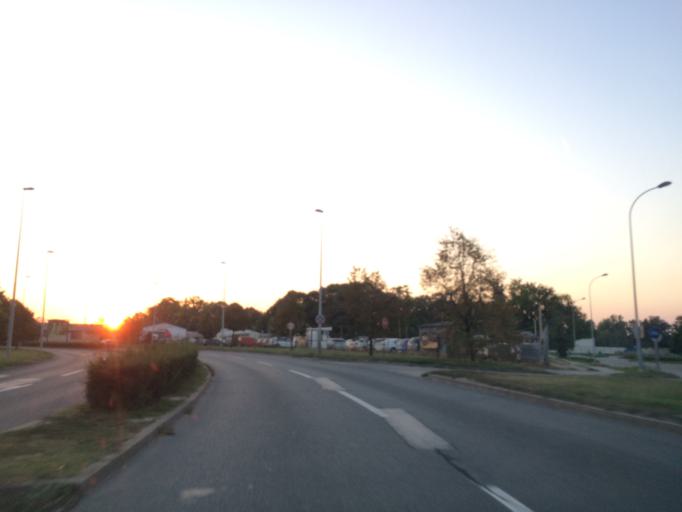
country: RS
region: Autonomna Pokrajina Vojvodina
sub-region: Juznobacki Okrug
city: Novi Sad
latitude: 45.2698
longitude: 19.8286
